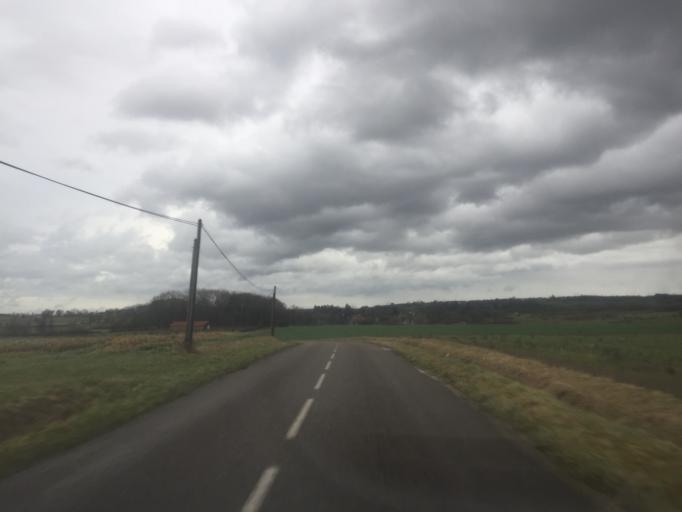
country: FR
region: Franche-Comte
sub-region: Departement de la Haute-Saone
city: Pesmes
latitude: 47.2189
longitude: 5.5064
